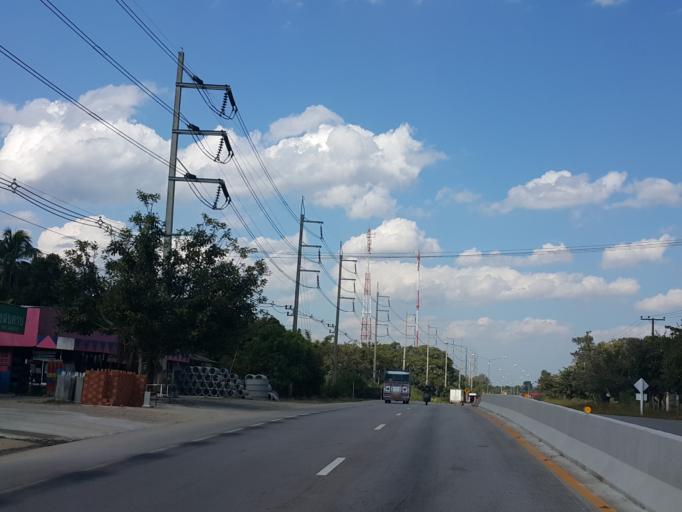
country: TH
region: Chiang Mai
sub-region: Amphoe Chiang Dao
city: Chiang Dao
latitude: 19.3081
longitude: 98.9570
